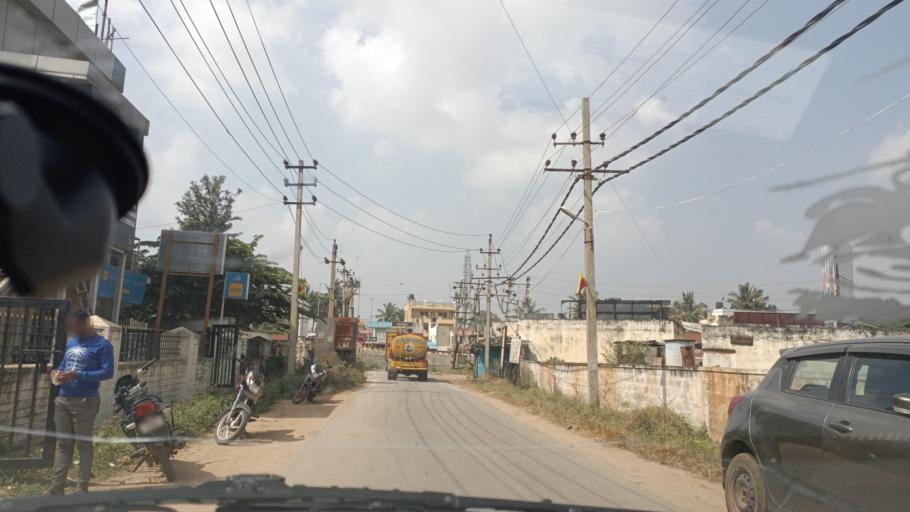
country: IN
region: Karnataka
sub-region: Bangalore Urban
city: Yelahanka
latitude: 13.1551
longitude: 77.6232
